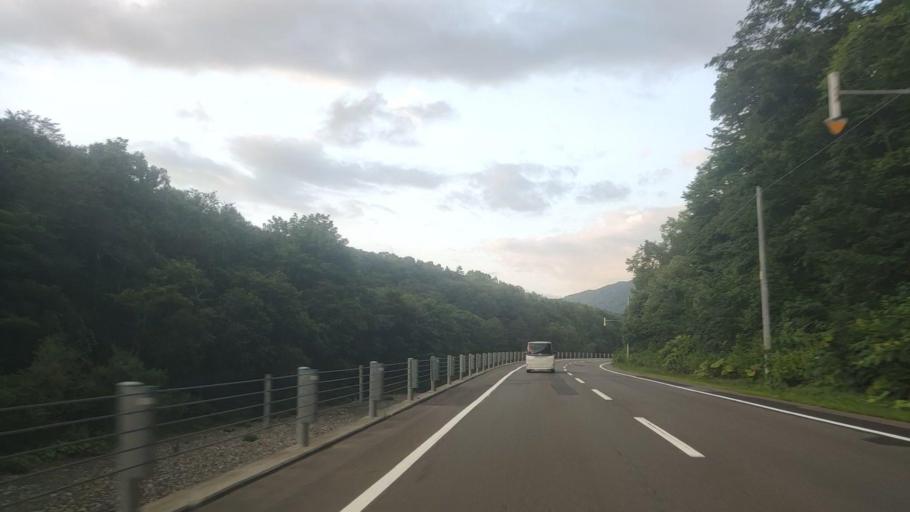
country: JP
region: Hokkaido
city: Ashibetsu
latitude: 43.3141
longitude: 142.1386
